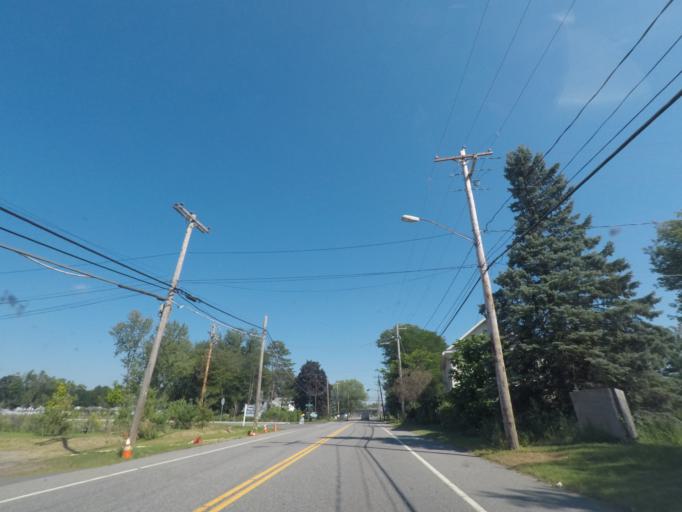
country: US
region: New York
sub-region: Albany County
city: Roessleville
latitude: 42.7387
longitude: -73.7878
